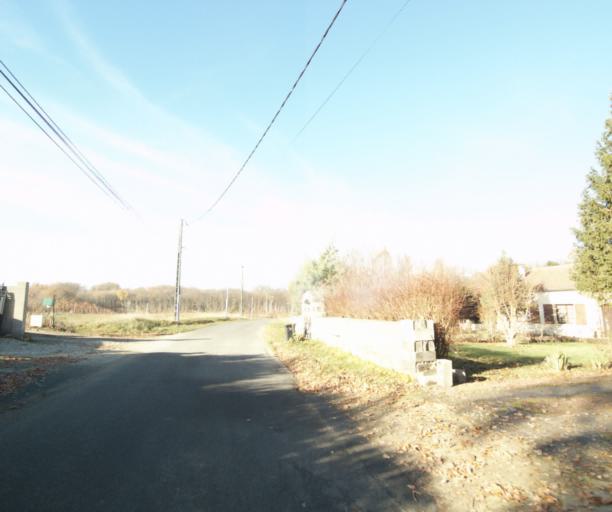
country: FR
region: Poitou-Charentes
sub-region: Departement de la Charente-Maritime
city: Burie
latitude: 45.7743
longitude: -0.4300
